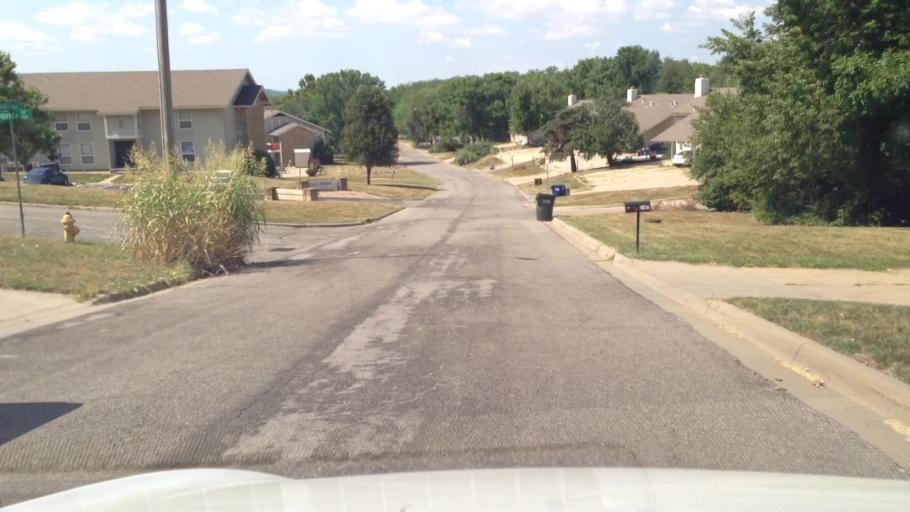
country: US
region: Kansas
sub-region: Douglas County
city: Lawrence
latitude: 38.9473
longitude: -95.2811
